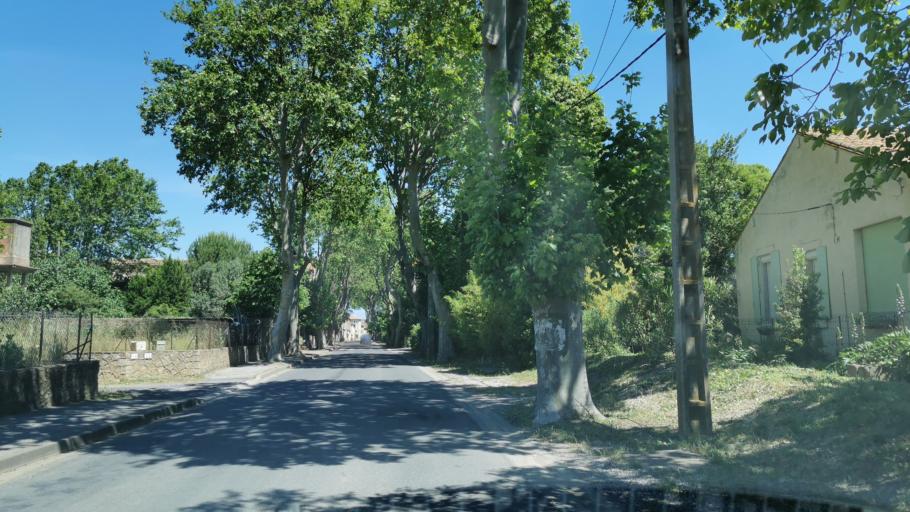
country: FR
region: Languedoc-Roussillon
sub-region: Departement de l'Aude
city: Canet
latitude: 43.2244
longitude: 2.8467
